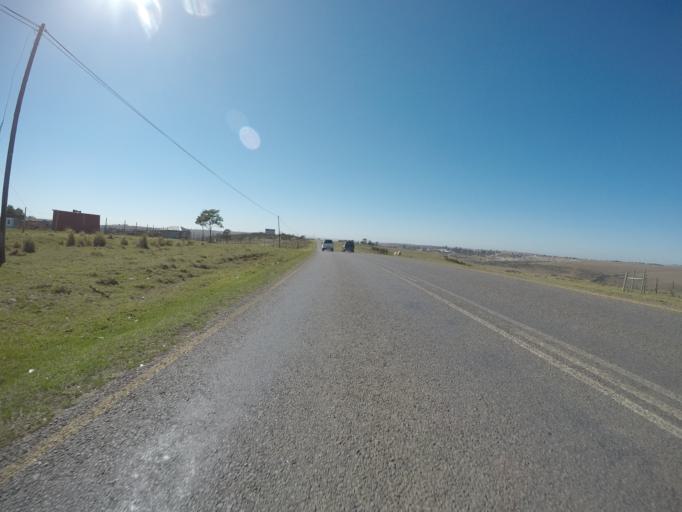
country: ZA
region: Eastern Cape
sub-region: OR Tambo District Municipality
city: Mthatha
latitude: -31.8003
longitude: 28.7469
